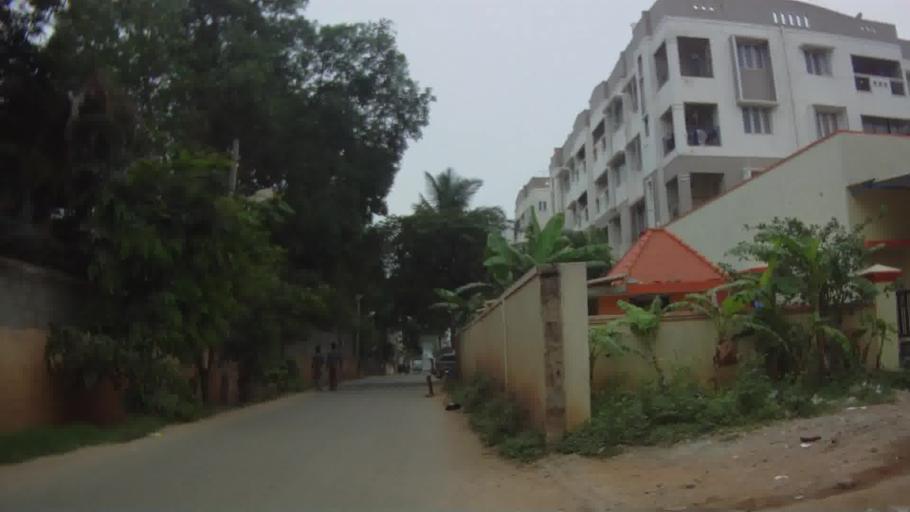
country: IN
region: Karnataka
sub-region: Bangalore Urban
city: Bangalore
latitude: 12.9574
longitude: 77.7219
